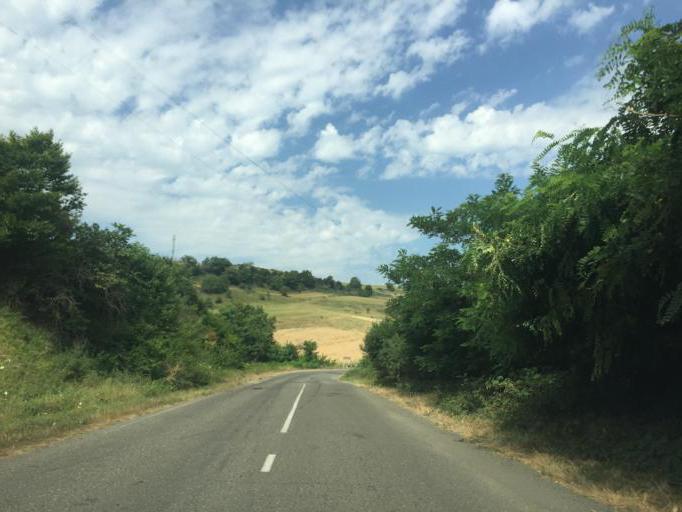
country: AZ
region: Xocali
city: Xocali
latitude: 39.9766
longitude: 46.7038
